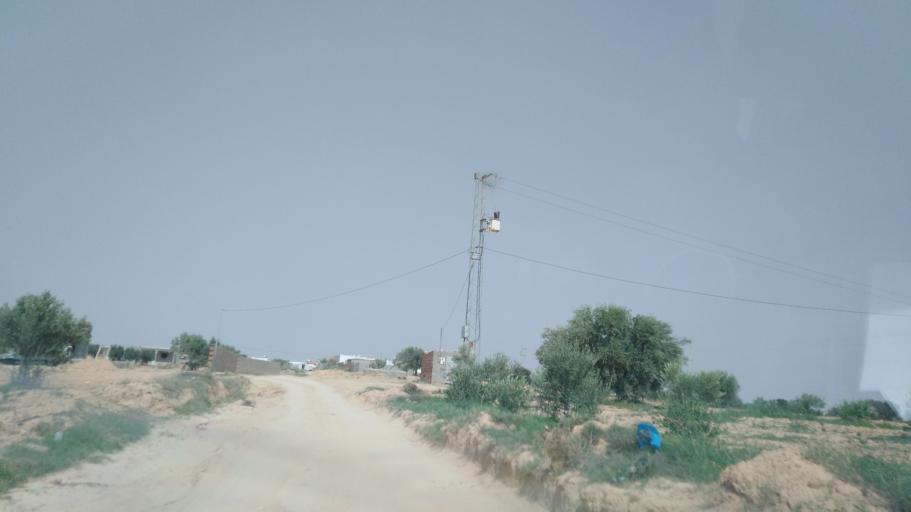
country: TN
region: Safaqis
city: Sfax
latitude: 34.6241
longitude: 10.5766
